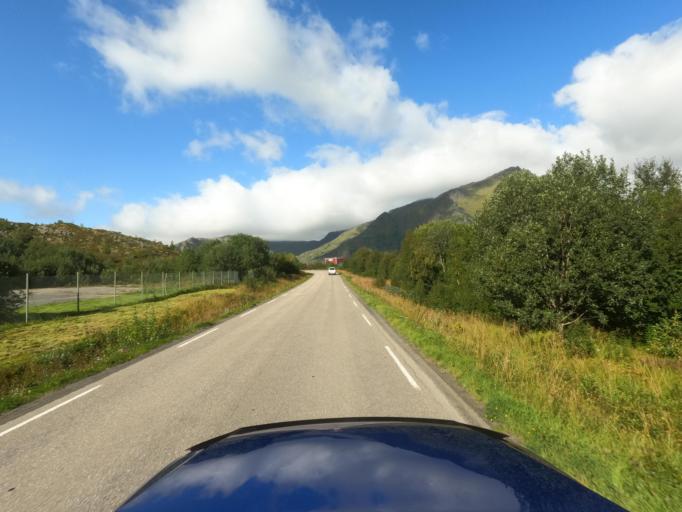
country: NO
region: Nordland
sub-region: Vestvagoy
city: Evjen
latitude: 68.1529
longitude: 13.8342
